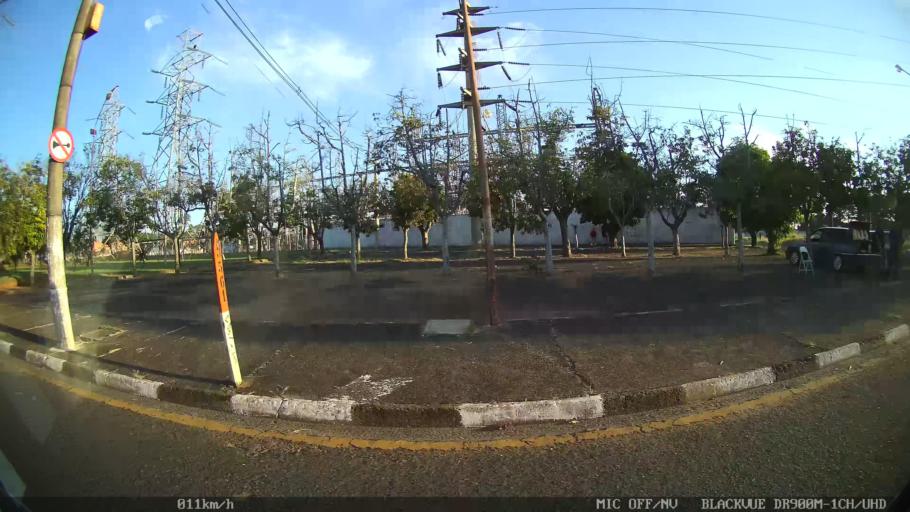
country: BR
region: Sao Paulo
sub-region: Franca
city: Franca
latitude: -20.5145
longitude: -47.3800
